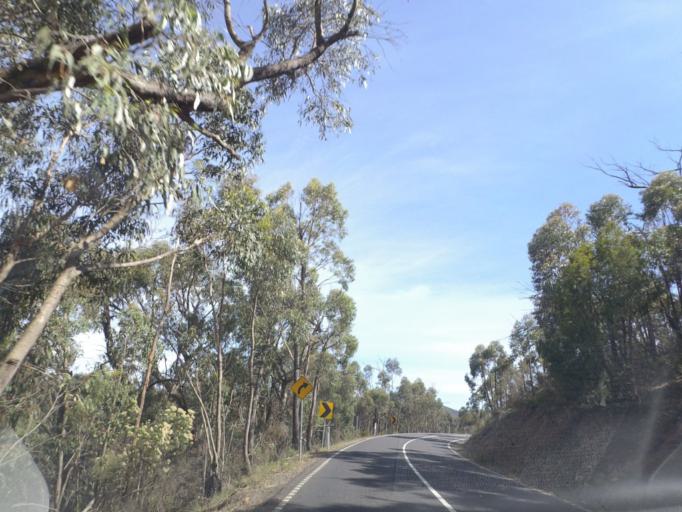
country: AU
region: Victoria
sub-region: Nillumbik
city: Saint Andrews
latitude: -37.5616
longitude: 145.3199
